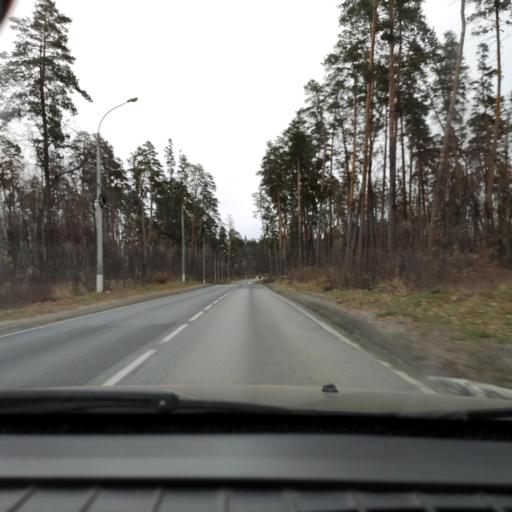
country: RU
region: Samara
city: Tol'yatti
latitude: 53.4923
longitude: 49.3015
